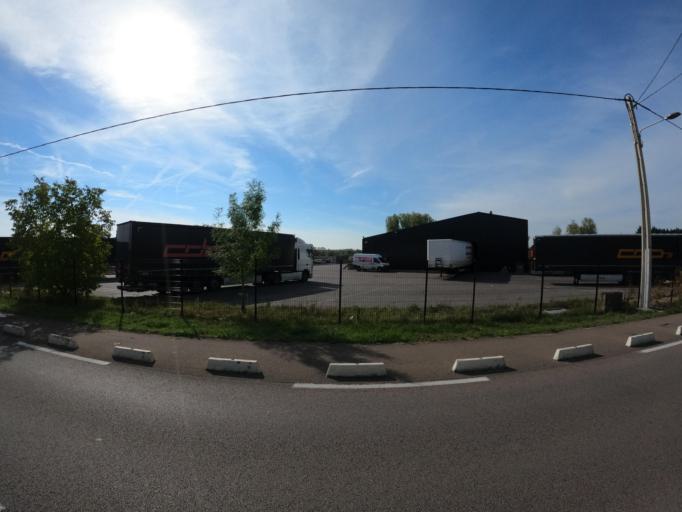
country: FR
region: Bourgogne
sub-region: Departement de Saone-et-Loire
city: Saint-Marcel
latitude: 46.7827
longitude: 4.9139
